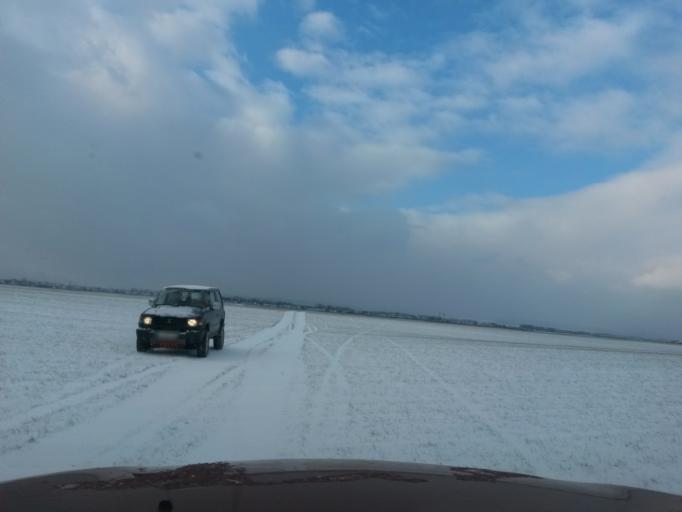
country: SK
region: Kosicky
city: Kosice
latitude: 48.6345
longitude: 21.3338
